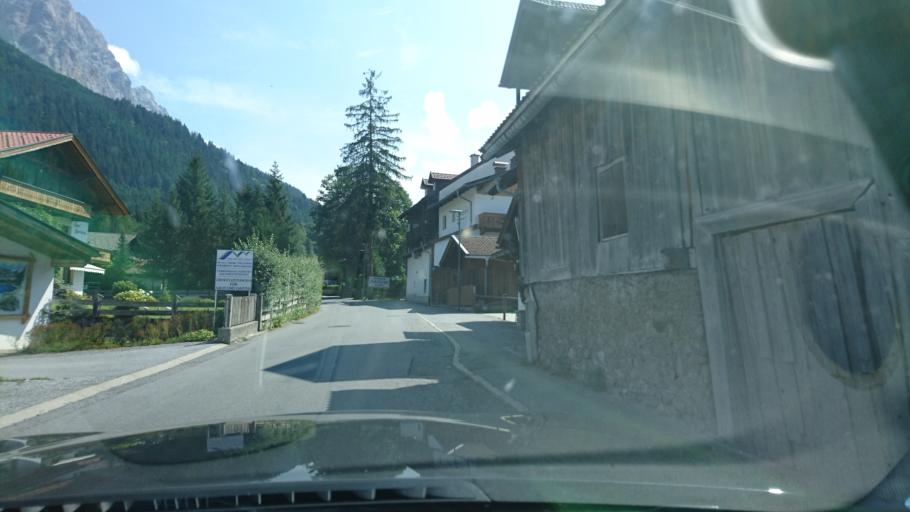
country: AT
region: Tyrol
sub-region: Politischer Bezirk Reutte
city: Ehrwald
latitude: 47.3954
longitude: 10.9240
